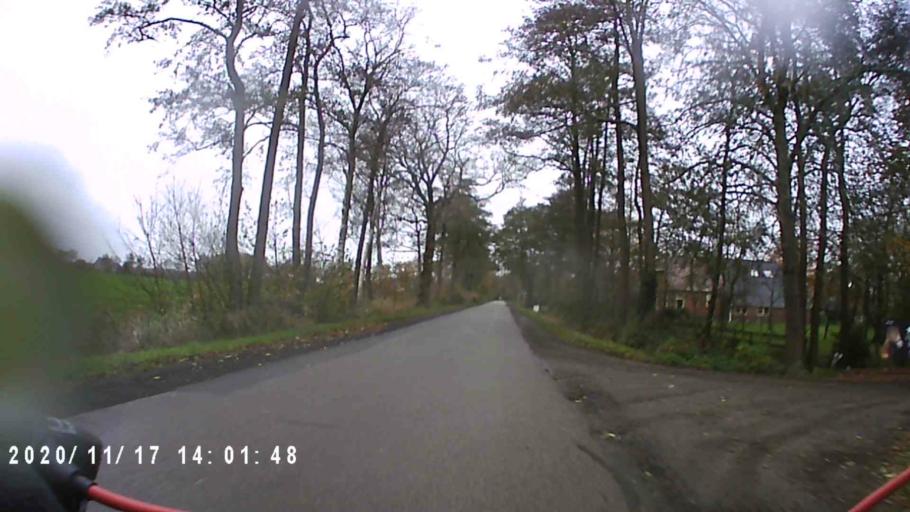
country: NL
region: Groningen
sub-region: Gemeente Zuidhorn
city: Grijpskerk
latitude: 53.2302
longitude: 6.3391
